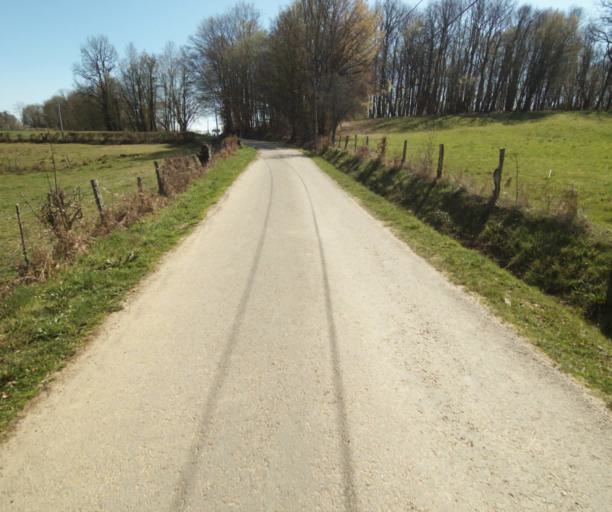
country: FR
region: Limousin
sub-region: Departement de la Correze
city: Chameyrat
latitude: 45.2528
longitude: 1.7064
